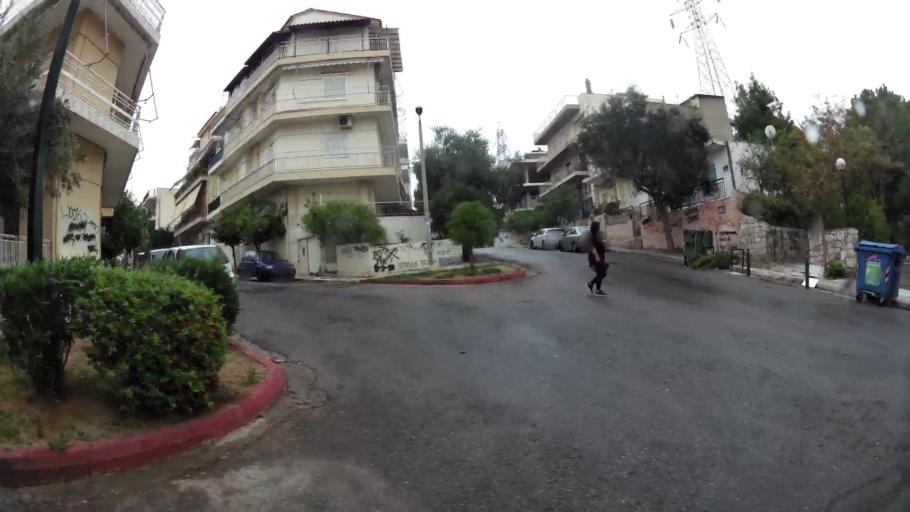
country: GR
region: Attica
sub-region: Nomarchia Athinas
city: Agia Varvara
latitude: 37.9893
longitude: 23.6536
